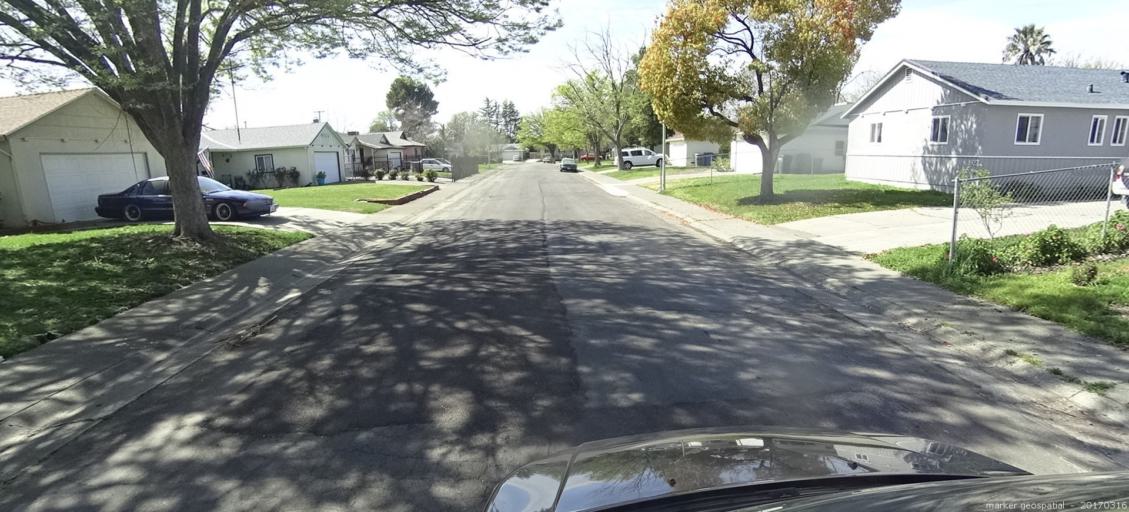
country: US
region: California
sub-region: Sacramento County
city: Parkway
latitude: 38.4781
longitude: -121.4937
